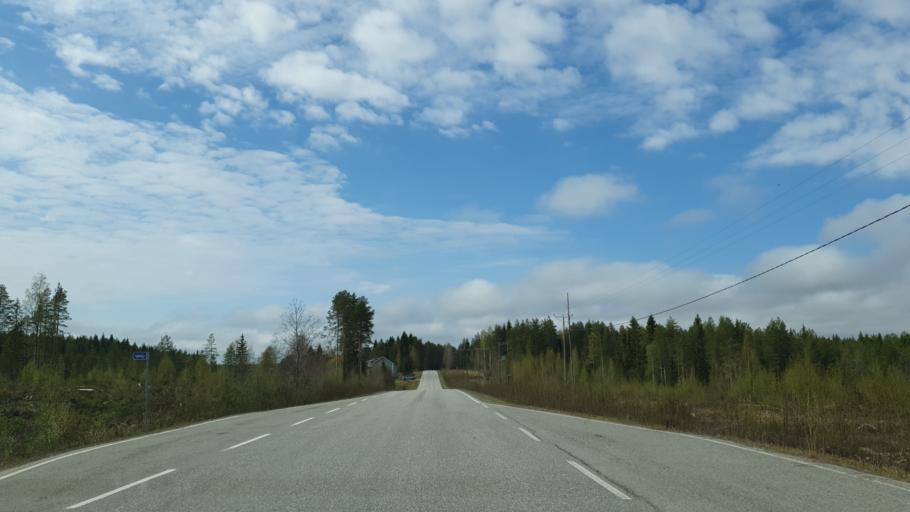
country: FI
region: Kainuu
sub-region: Kehys-Kainuu
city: Kuhmo
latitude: 64.1219
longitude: 29.6655
